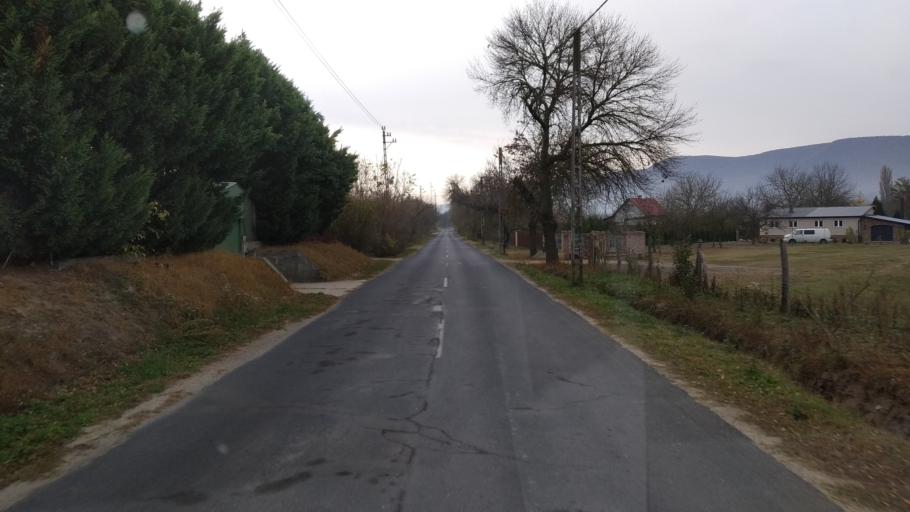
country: HU
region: Pest
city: Tahitotfalu
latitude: 47.7701
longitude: 19.0879
